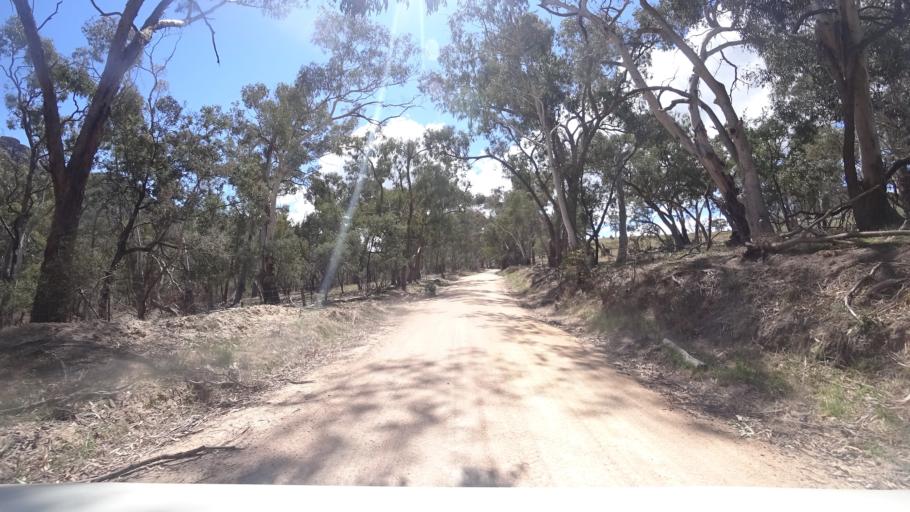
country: AU
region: New South Wales
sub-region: Oberon
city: Oberon
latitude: -33.5471
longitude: 149.9318
